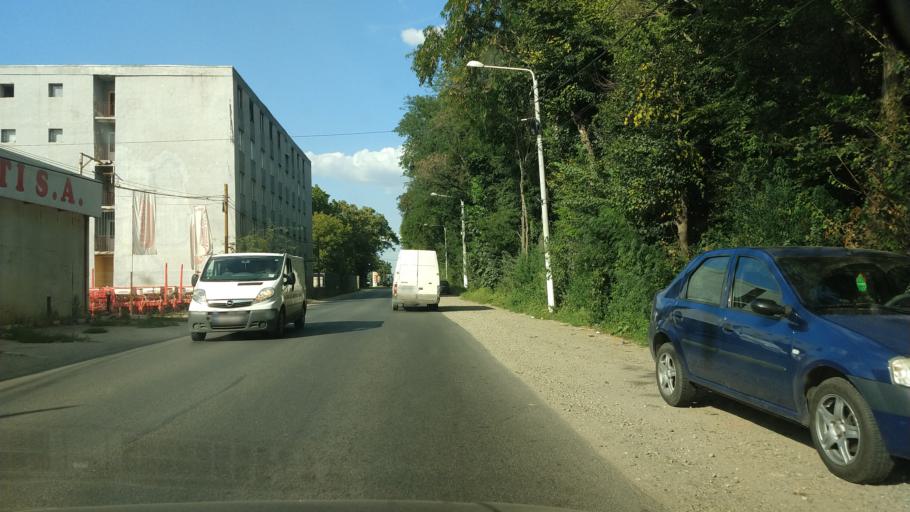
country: RO
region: Ilfov
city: Stefanestii de Jos
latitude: 44.5198
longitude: 26.1935
